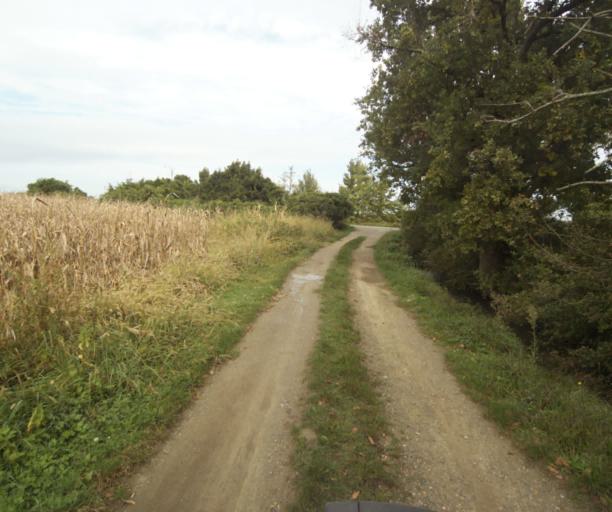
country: FR
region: Midi-Pyrenees
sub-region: Departement du Tarn-et-Garonne
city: Finhan
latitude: 43.9148
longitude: 1.2382
